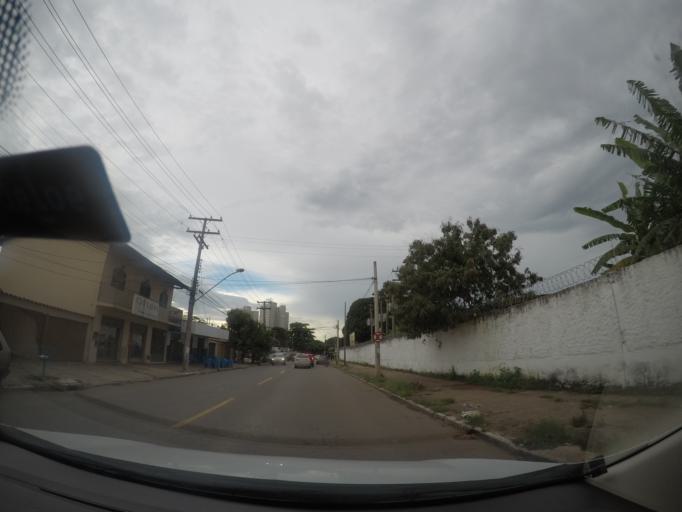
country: BR
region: Goias
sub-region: Goiania
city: Goiania
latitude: -16.6569
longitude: -49.2489
